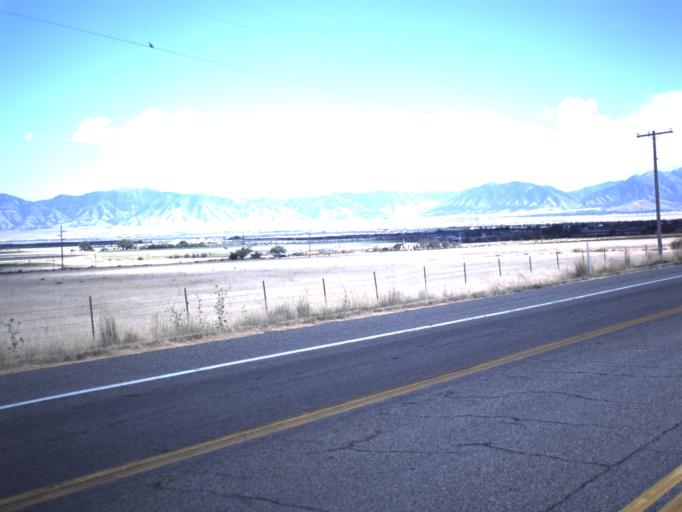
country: US
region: Utah
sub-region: Tooele County
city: Grantsville
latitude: 40.6299
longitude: -112.5126
